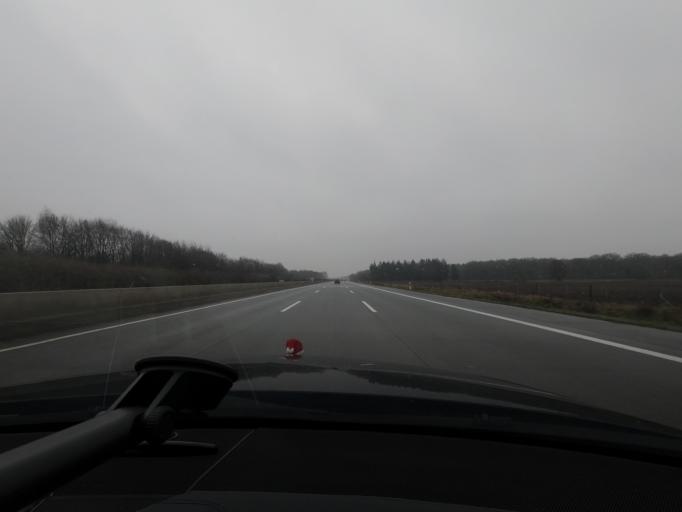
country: DE
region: Schleswig-Holstein
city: Padenstedt
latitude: 54.0278
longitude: 9.9323
